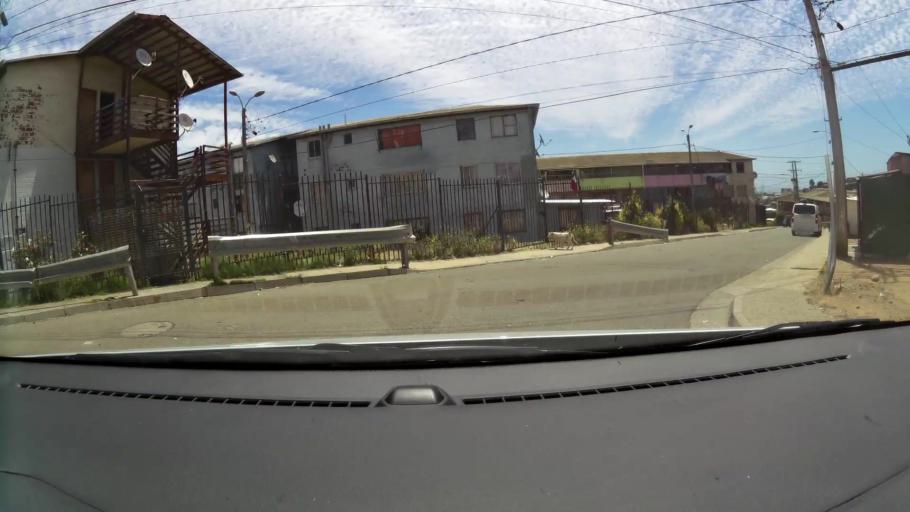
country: CL
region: Valparaiso
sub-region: Provincia de Valparaiso
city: Vina del Mar
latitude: -33.0544
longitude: -71.5734
